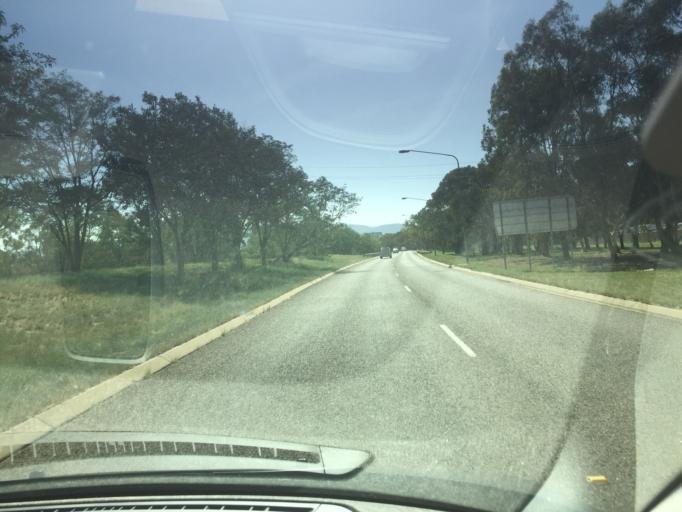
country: AU
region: Australian Capital Territory
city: Macarthur
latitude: -35.4235
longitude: 149.0864
